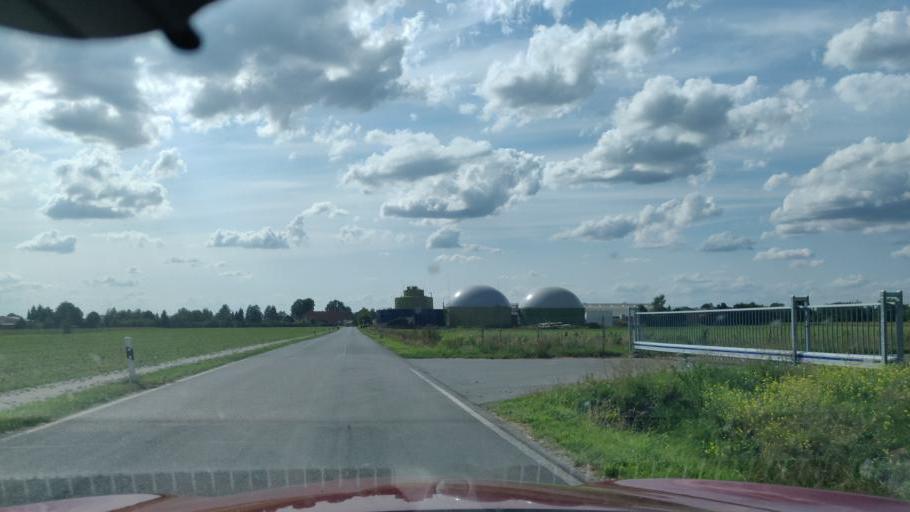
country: DE
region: Saxony
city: Schildau
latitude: 51.4821
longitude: 12.9132
